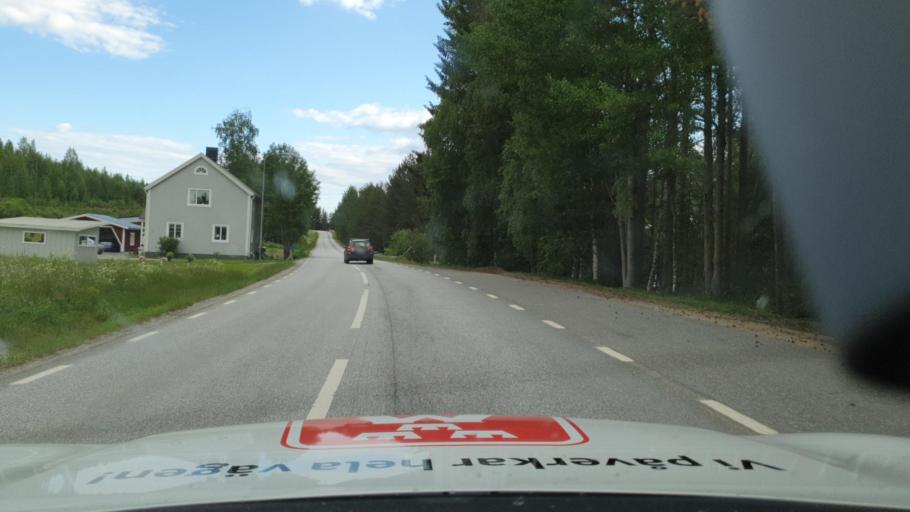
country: SE
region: Vaesterbotten
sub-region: Vindelns Kommun
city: Vindeln
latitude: 64.2257
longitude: 19.7072
